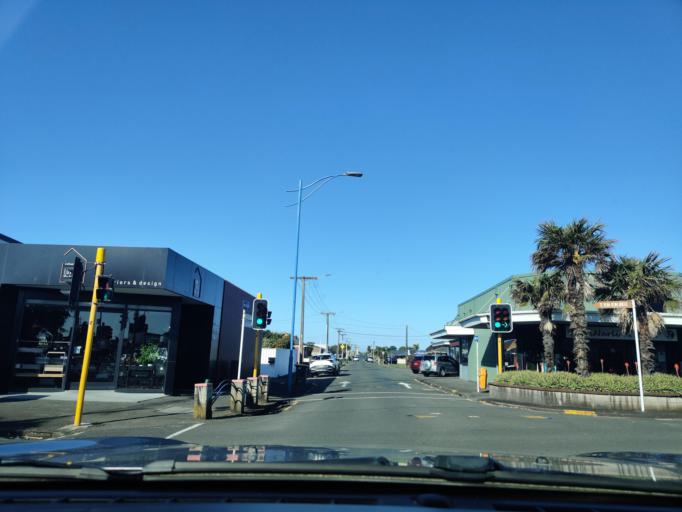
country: NZ
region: Taranaki
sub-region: New Plymouth District
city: New Plymouth
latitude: -39.0493
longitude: 174.1022
